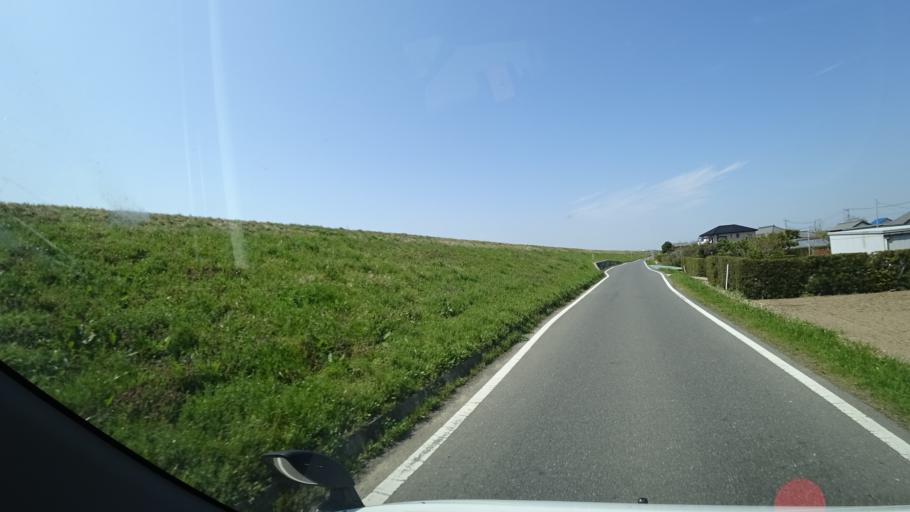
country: JP
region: Ibaraki
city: Edosaki
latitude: 35.8669
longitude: 140.3123
